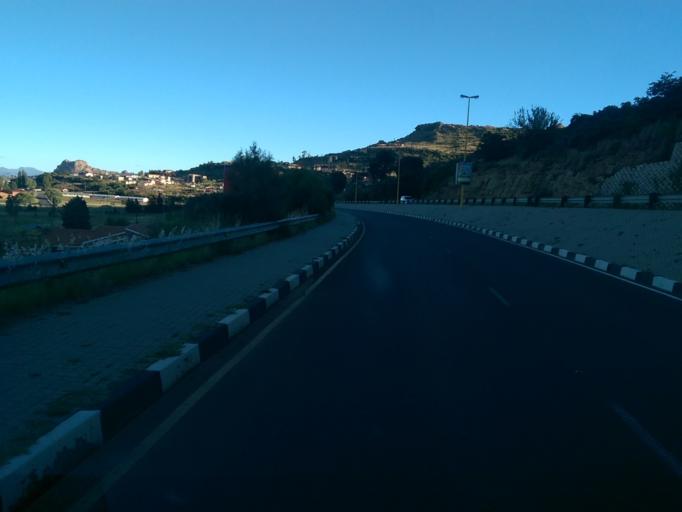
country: LS
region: Maseru
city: Maseru
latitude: -29.3222
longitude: 27.4953
